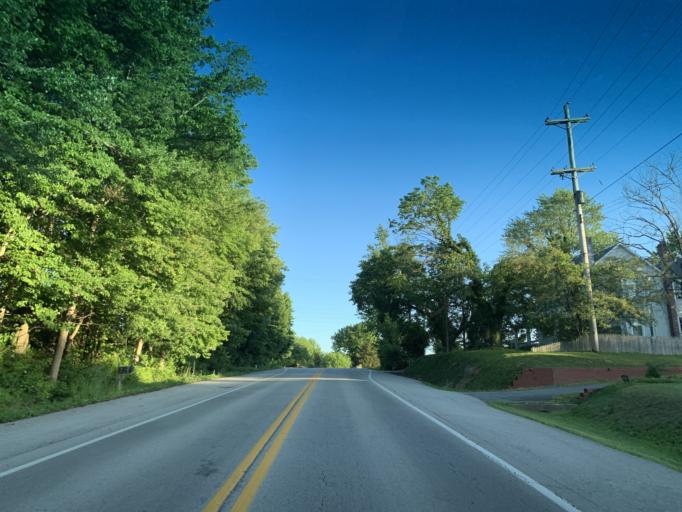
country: US
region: Maryland
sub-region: Cecil County
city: Elkton
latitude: 39.6448
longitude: -75.8125
